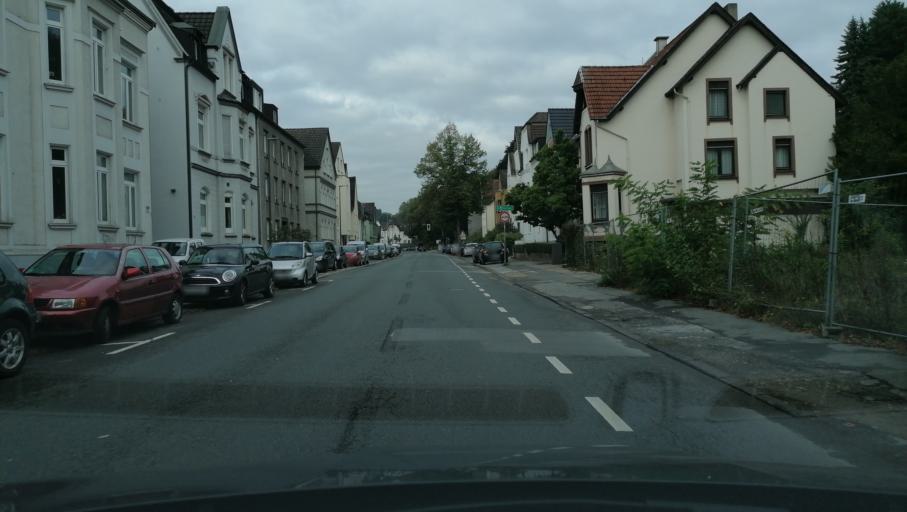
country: DE
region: North Rhine-Westphalia
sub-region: Regierungsbezirk Munster
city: Recklinghausen
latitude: 51.6184
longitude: 7.1918
